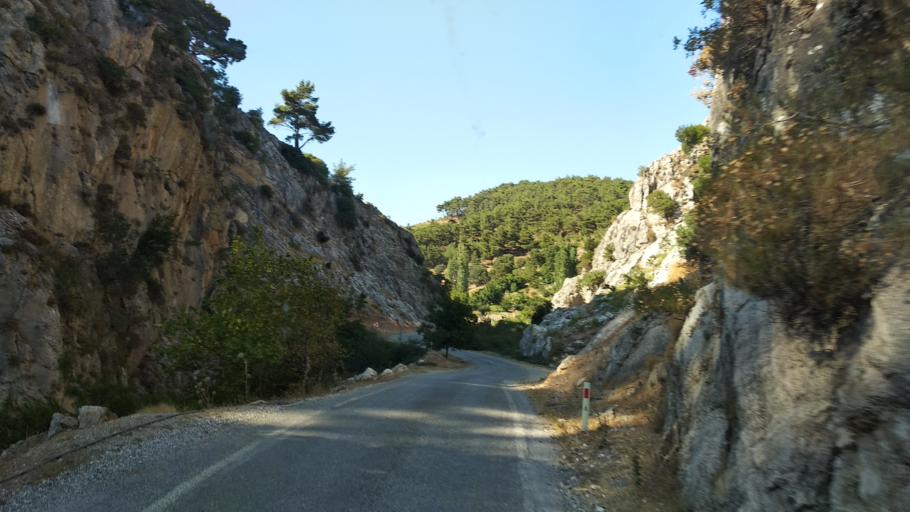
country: TR
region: Izmir
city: Gaziemir
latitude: 38.3223
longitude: 26.9573
